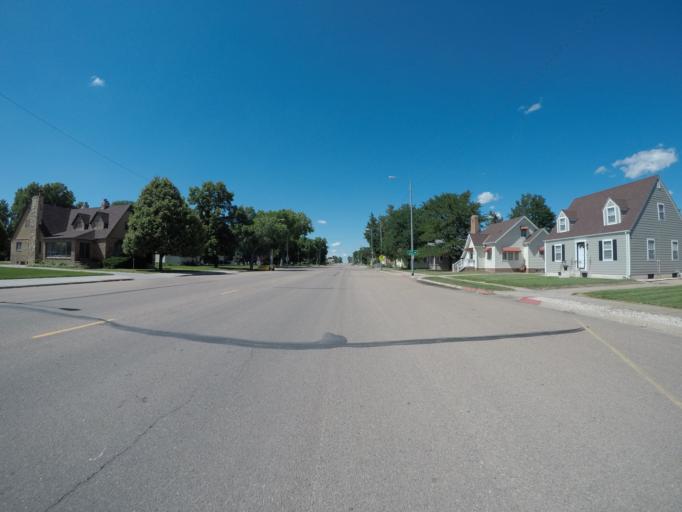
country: US
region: Nebraska
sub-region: Chase County
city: Imperial
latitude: 40.5193
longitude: -101.6431
